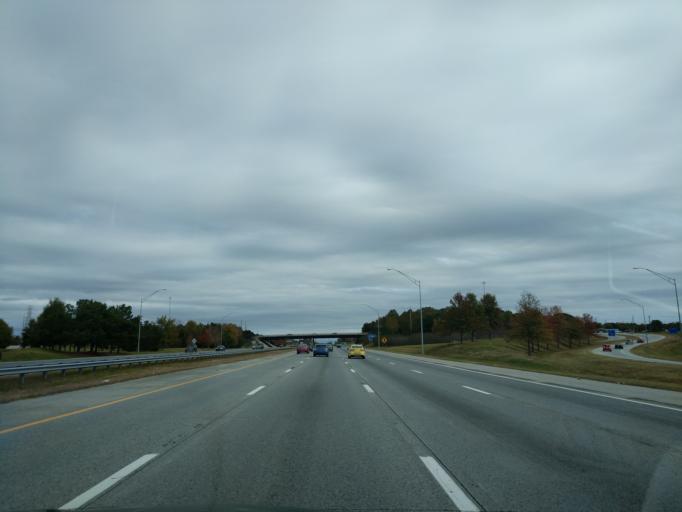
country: US
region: North Carolina
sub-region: Rowan County
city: Salisbury
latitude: 35.6309
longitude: -80.4942
